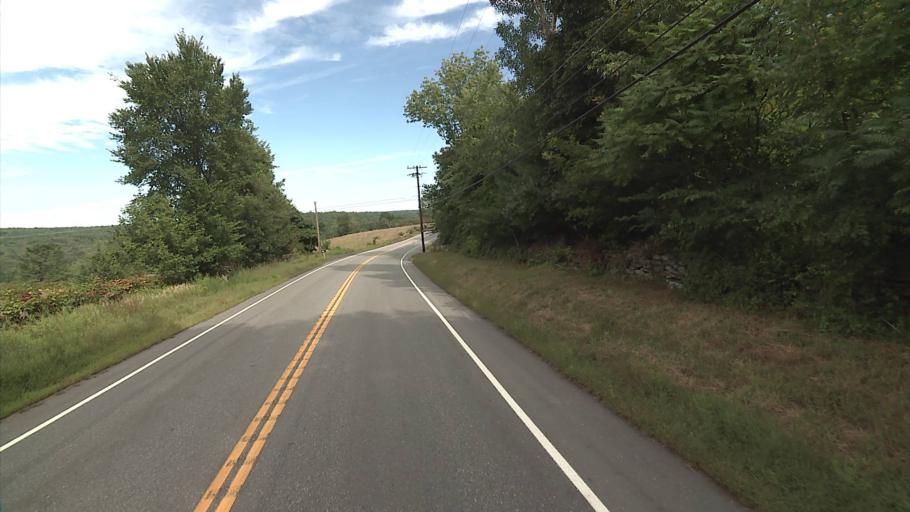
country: US
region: Connecticut
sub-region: Tolland County
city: South Coventry
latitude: 41.8134
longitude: -72.3084
